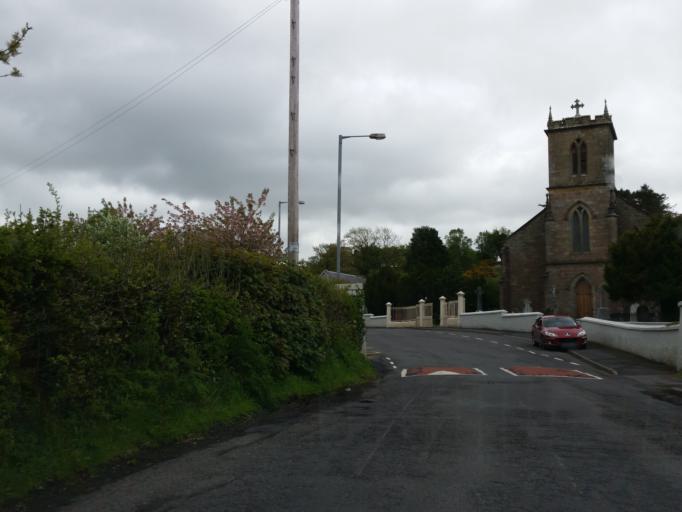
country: GB
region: Northern Ireland
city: Lisnaskea
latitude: 54.3177
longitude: -7.4007
